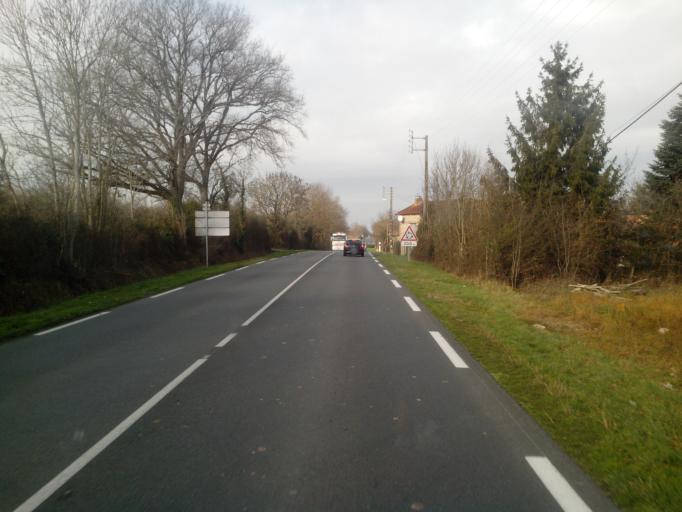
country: FR
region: Limousin
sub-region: Departement de la Haute-Vienne
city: Bussiere-Poitevine
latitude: 46.2671
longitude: 0.8663
